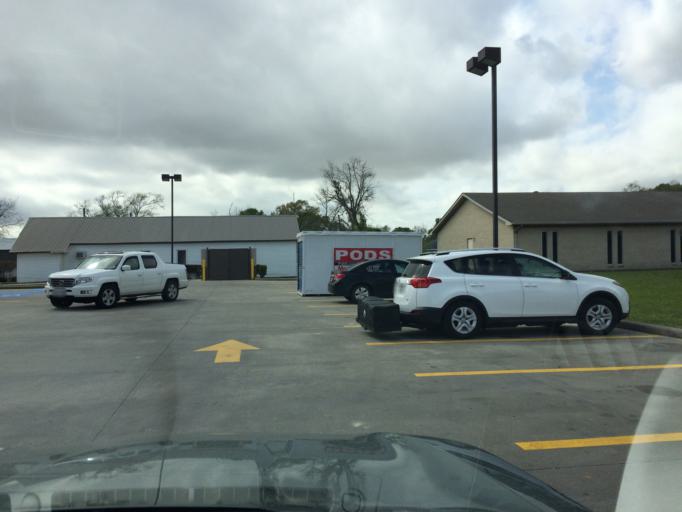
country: US
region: Louisiana
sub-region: Calcasieu Parish
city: Westlake
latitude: 30.2429
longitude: -93.2583
